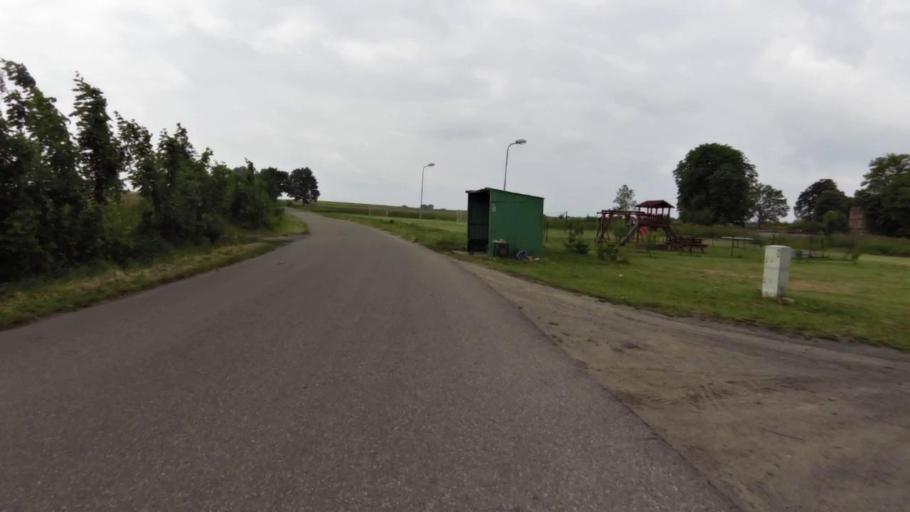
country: PL
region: West Pomeranian Voivodeship
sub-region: Powiat kamienski
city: Wolin
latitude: 53.8262
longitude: 14.6197
